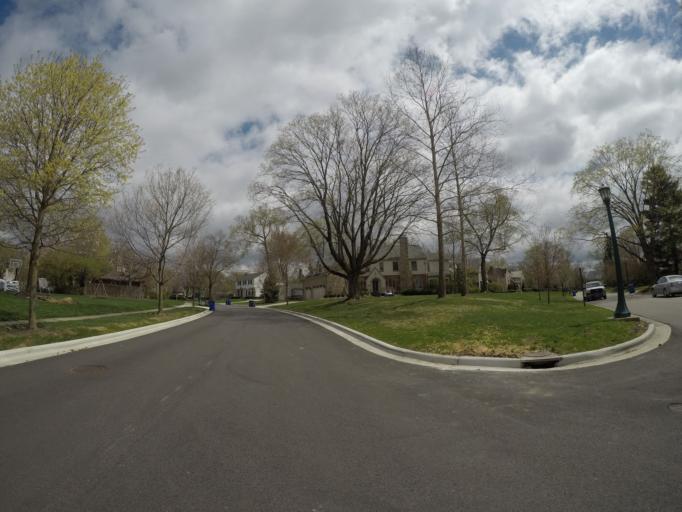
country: US
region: Ohio
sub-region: Franklin County
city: Upper Arlington
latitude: 39.9998
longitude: -83.0669
